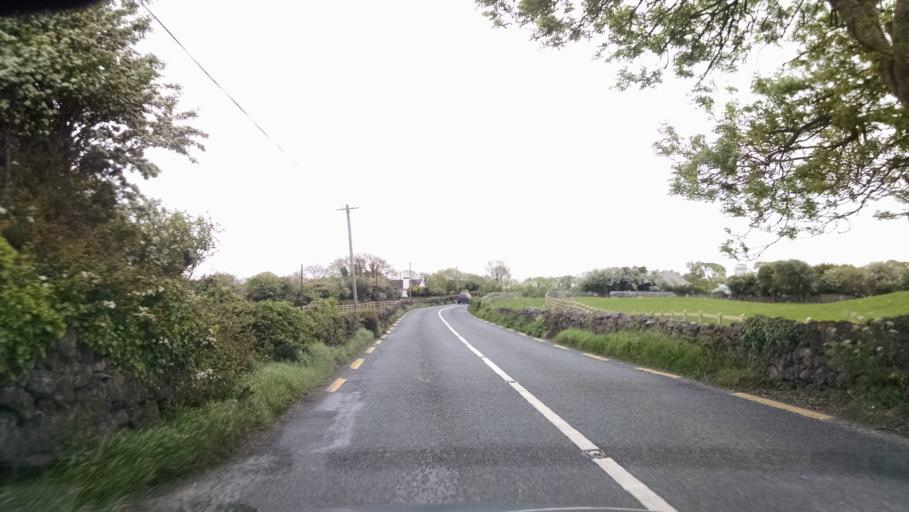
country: IE
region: Connaught
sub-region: County Galway
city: Moycullen
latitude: 53.4376
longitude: -9.0639
